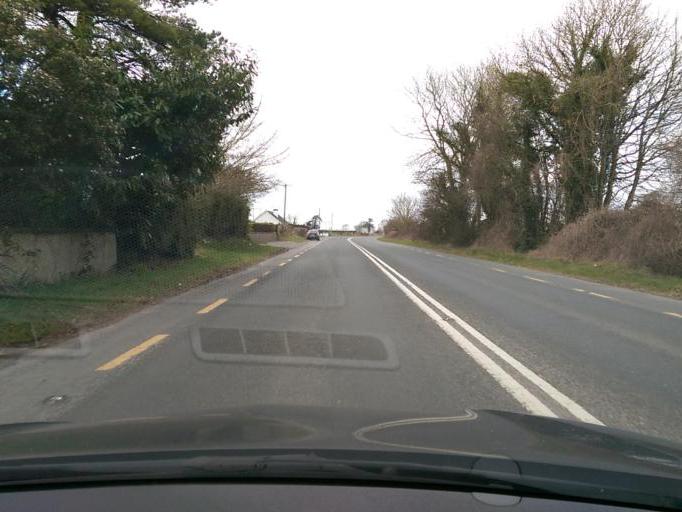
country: IE
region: Leinster
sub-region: An Iarmhi
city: Athlone
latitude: 53.3870
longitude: -7.9920
